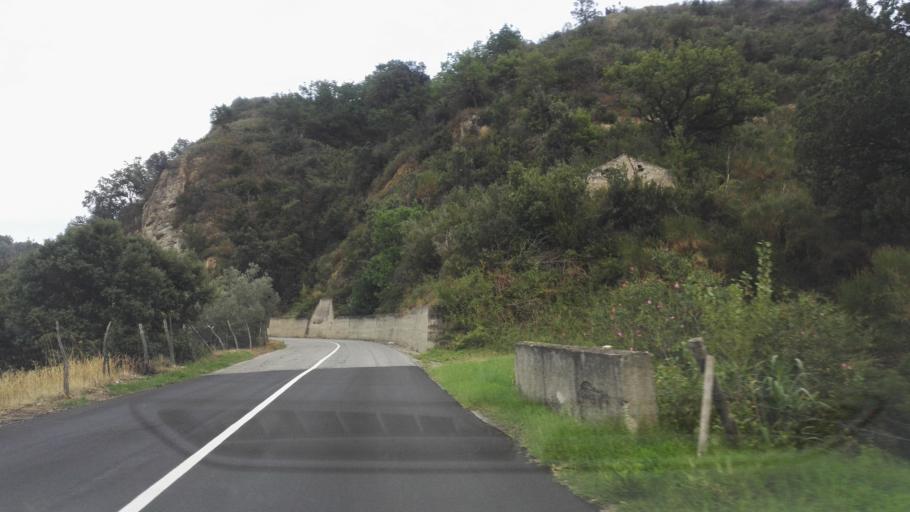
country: IT
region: Calabria
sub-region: Provincia di Reggio Calabria
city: Caulonia
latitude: 38.4008
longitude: 16.4117
